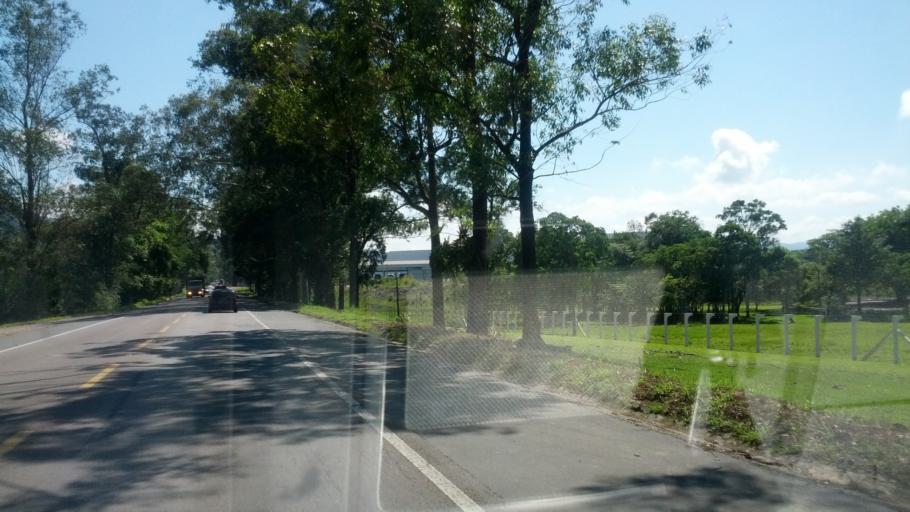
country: BR
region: Santa Catarina
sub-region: Rio Do Sul
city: Rio do Sul
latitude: -27.1801
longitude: -49.5975
